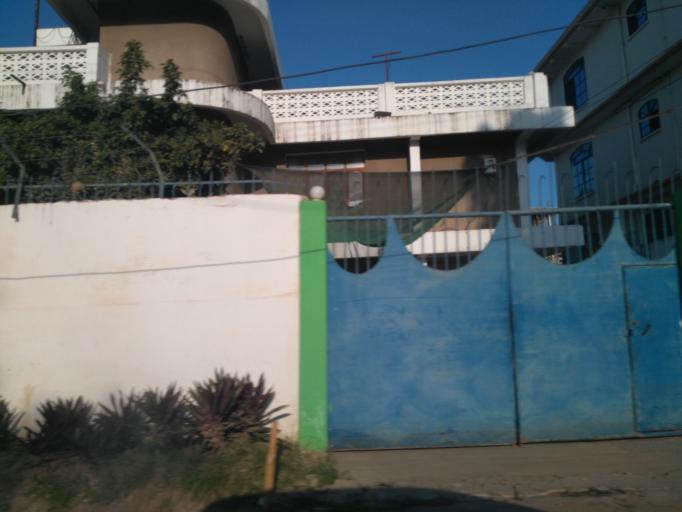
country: TZ
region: Dar es Salaam
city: Magomeni
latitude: -6.7616
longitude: 39.2650
